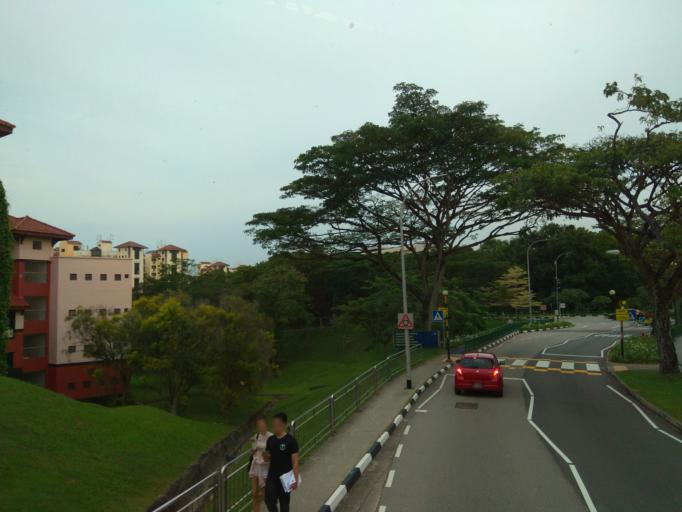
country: MY
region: Johor
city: Johor Bahru
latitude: 1.3501
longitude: 103.6843
